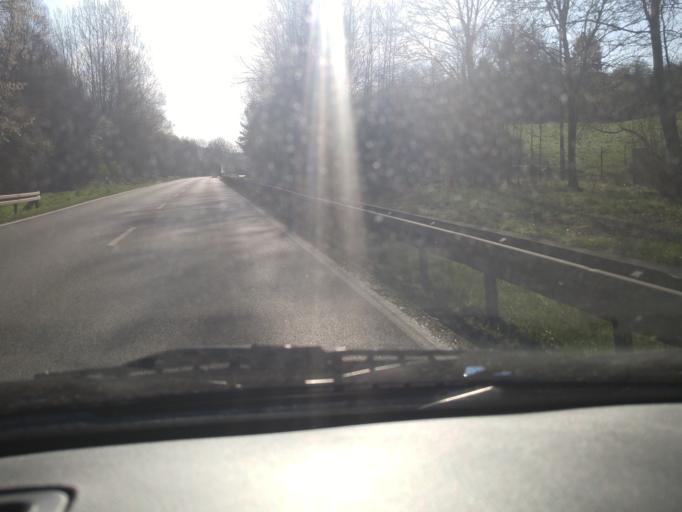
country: DE
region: Hesse
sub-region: Regierungsbezirk Giessen
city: Lauterbach
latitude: 50.6401
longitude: 9.4171
